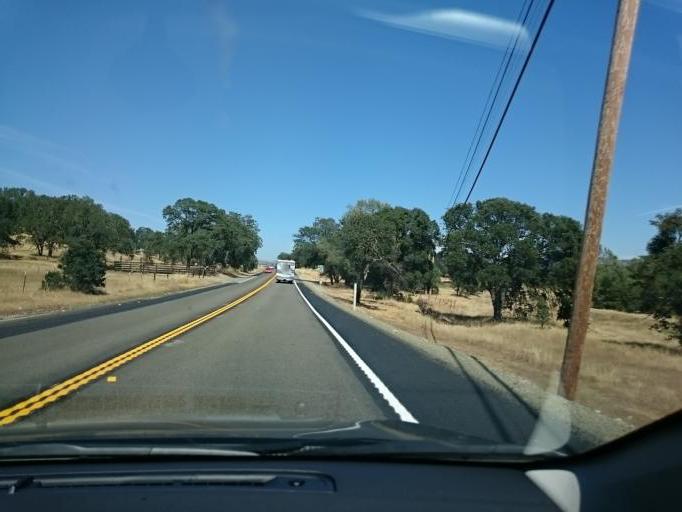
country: US
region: California
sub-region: Calaveras County
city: Valley Springs
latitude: 38.1848
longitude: -120.8396
